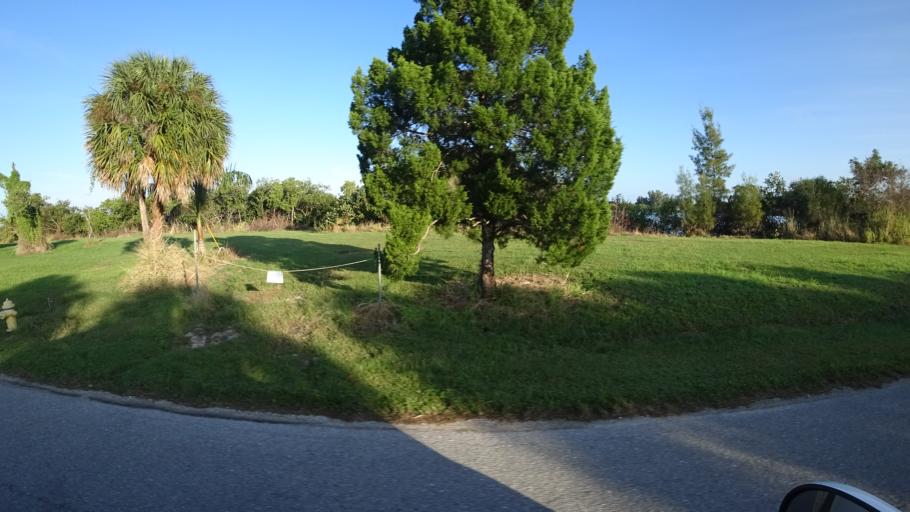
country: US
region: Florida
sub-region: Manatee County
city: Memphis
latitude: 27.5710
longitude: -82.5873
